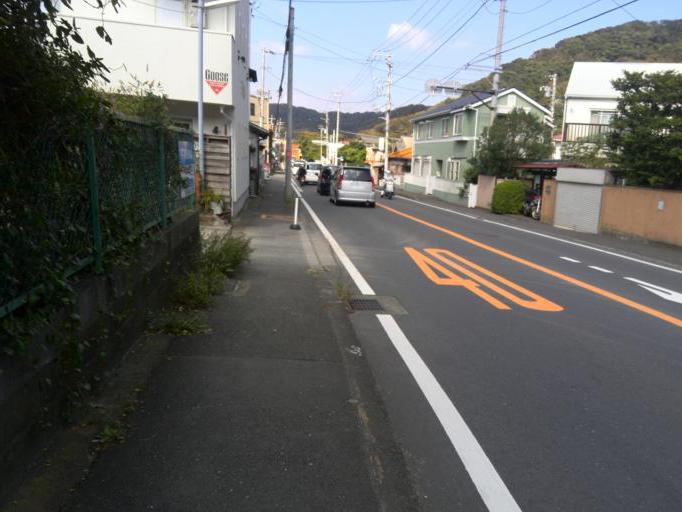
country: JP
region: Kanagawa
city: Hayama
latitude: 35.2762
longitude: 139.5789
